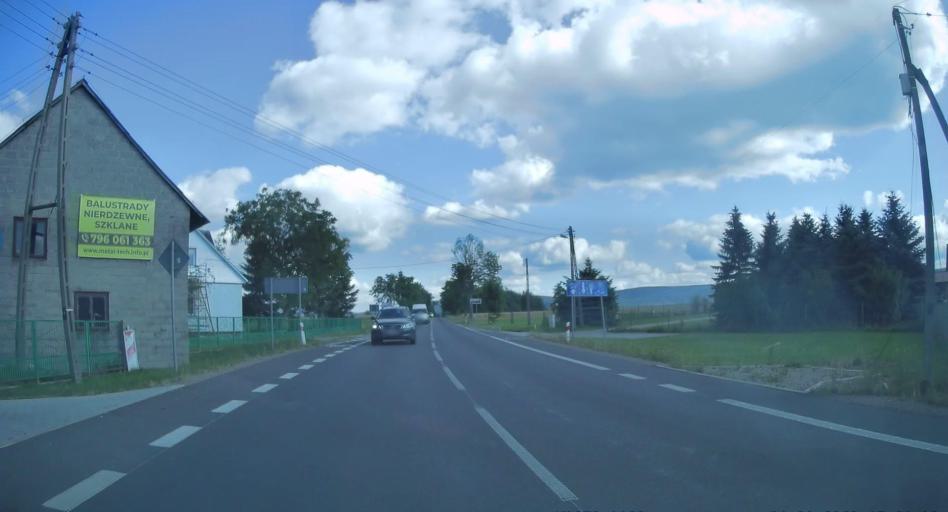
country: PL
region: Swietokrzyskie
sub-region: Powiat kielecki
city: Bodzentyn
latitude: 50.9305
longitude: 20.9791
